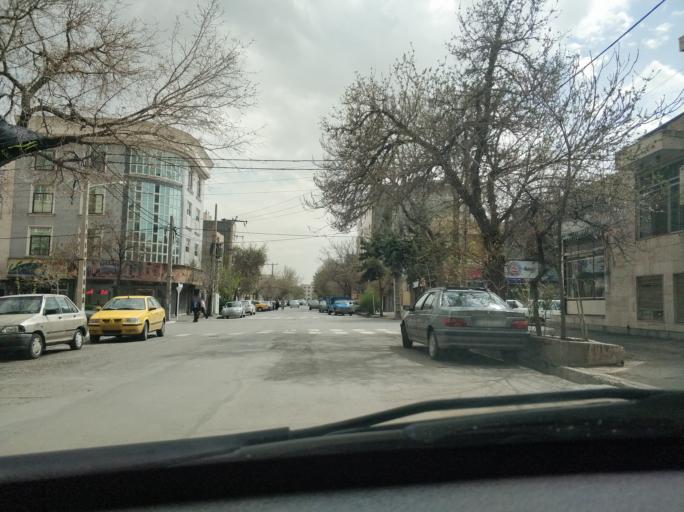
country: IR
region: Razavi Khorasan
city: Mashhad
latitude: 36.2755
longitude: 59.5721
